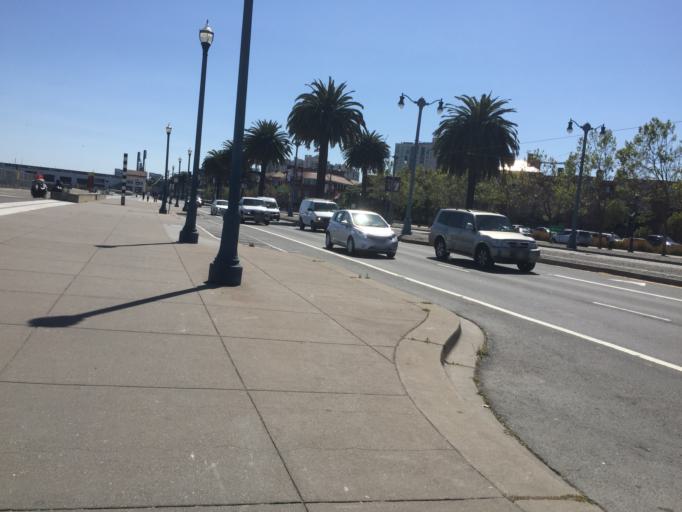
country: US
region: California
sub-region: San Francisco County
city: San Francisco
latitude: 37.7863
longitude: -122.3877
